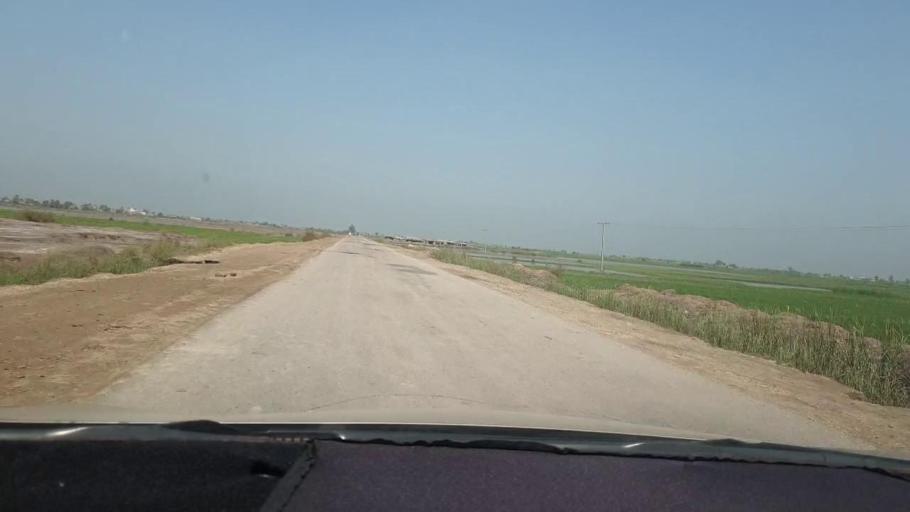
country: PK
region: Sindh
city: Miro Khan
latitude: 27.8325
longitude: 68.0137
